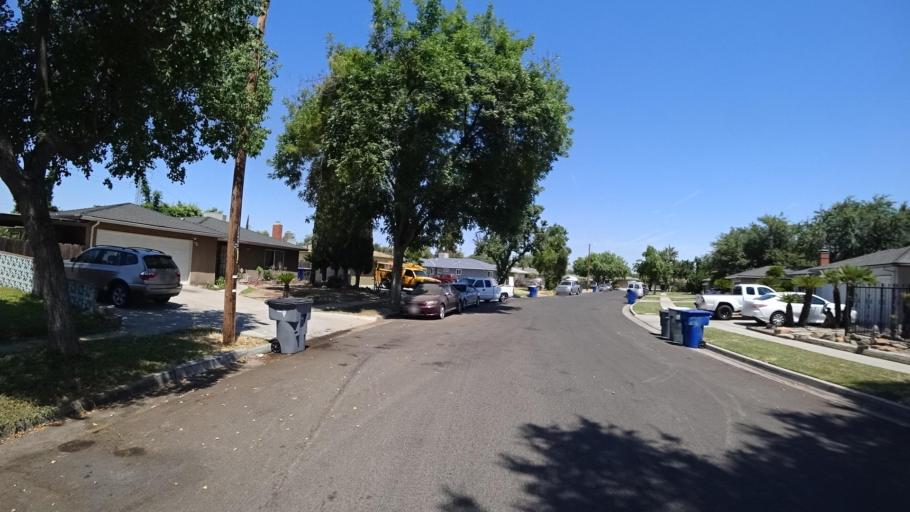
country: US
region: California
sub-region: Fresno County
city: Sunnyside
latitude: 36.7619
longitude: -119.7309
